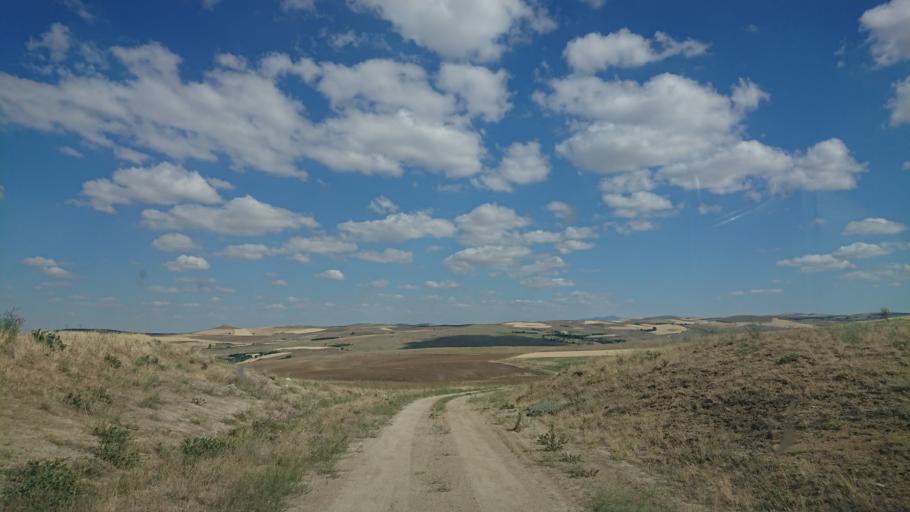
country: TR
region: Aksaray
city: Sariyahsi
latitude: 38.9305
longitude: 33.8482
